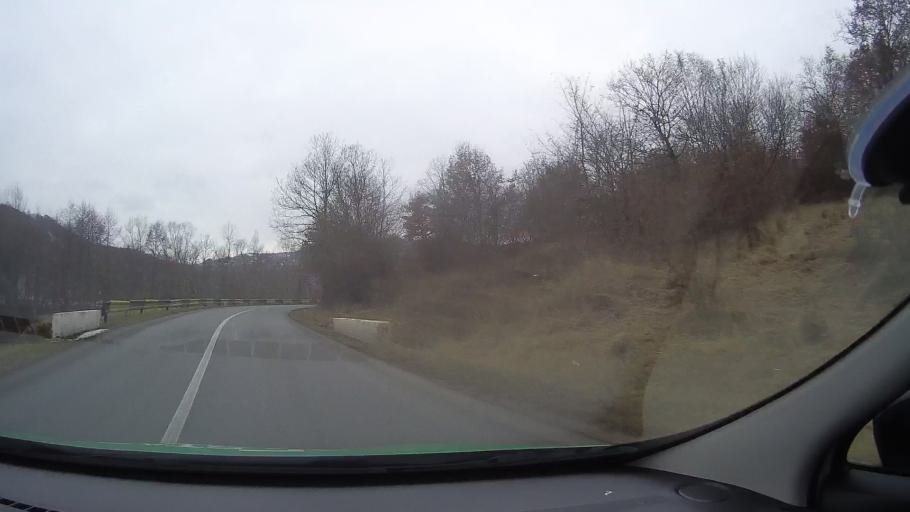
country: RO
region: Alba
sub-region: Comuna Metes
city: Metes
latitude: 46.1056
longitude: 23.4509
